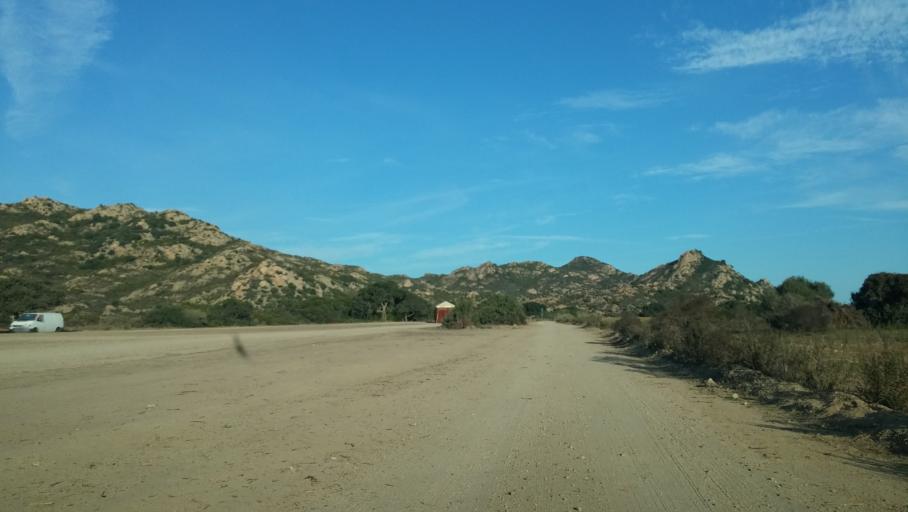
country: IT
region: Sardinia
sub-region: Provincia di Nuoro
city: La Caletta
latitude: 40.4807
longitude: 9.8075
